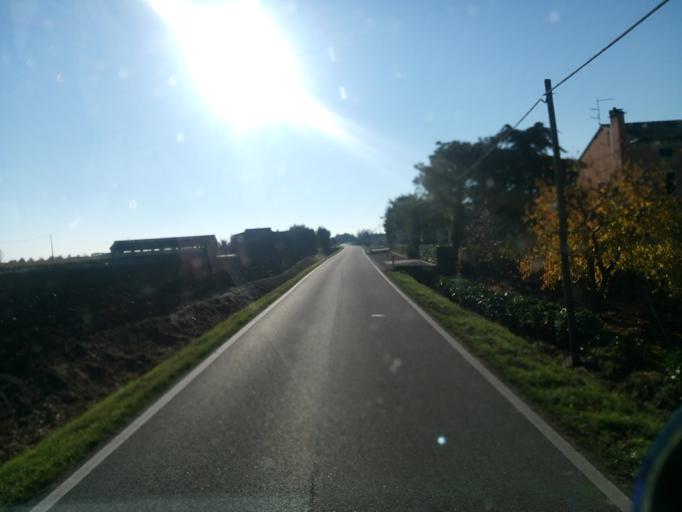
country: IT
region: Veneto
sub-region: Provincia di Vicenza
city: Asigliano Veneto
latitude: 45.3272
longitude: 11.4255
